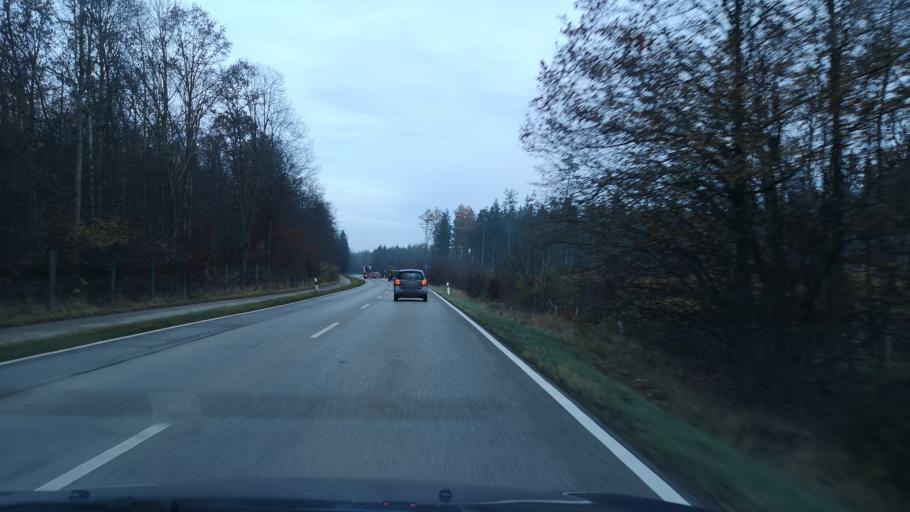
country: DE
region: Bavaria
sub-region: Upper Bavaria
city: Forstinning
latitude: 48.1430
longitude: 11.9254
